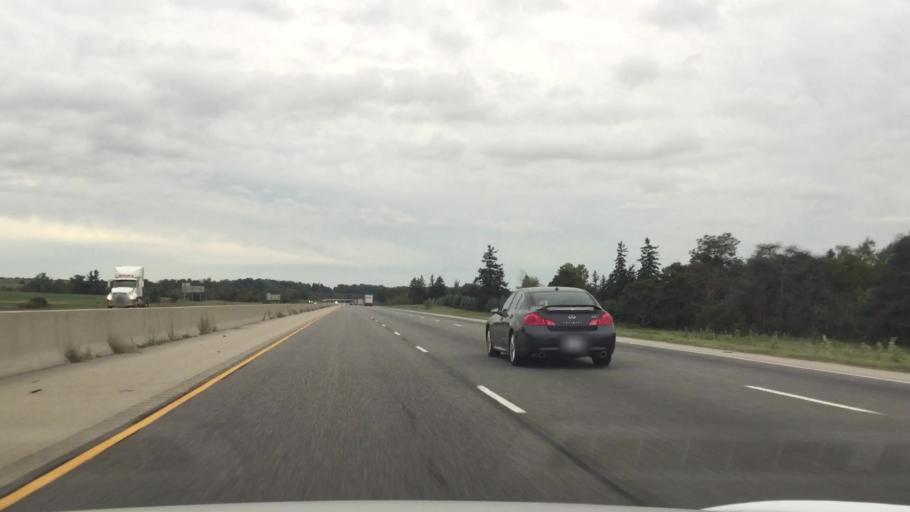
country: CA
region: Ontario
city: Kitchener
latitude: 43.3115
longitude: -80.4749
